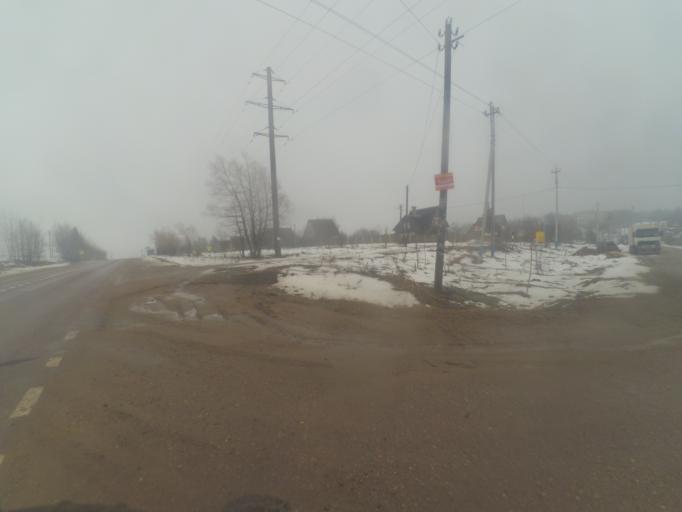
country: RU
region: Moskovskaya
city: Avtopoligon
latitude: 56.2672
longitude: 37.2467
